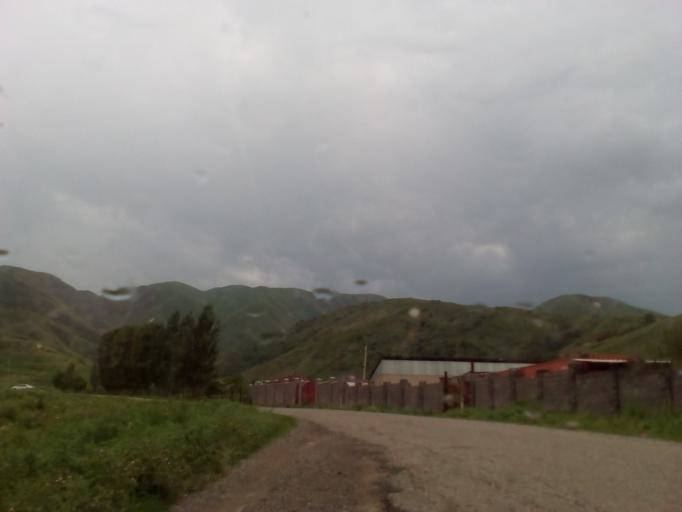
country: KZ
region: Almaty Oblysy
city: Burunday
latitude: 43.1519
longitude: 76.3852
